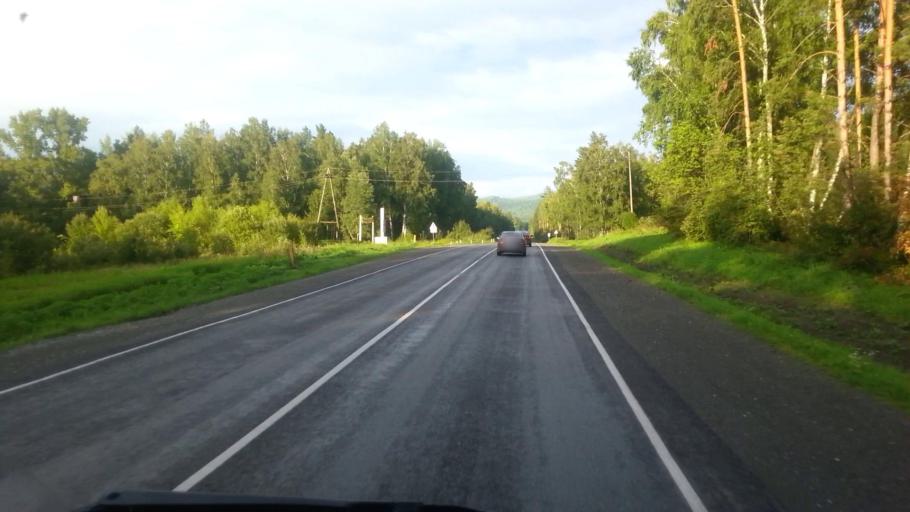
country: RU
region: Altay
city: Souzga
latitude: 51.8744
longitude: 85.8028
